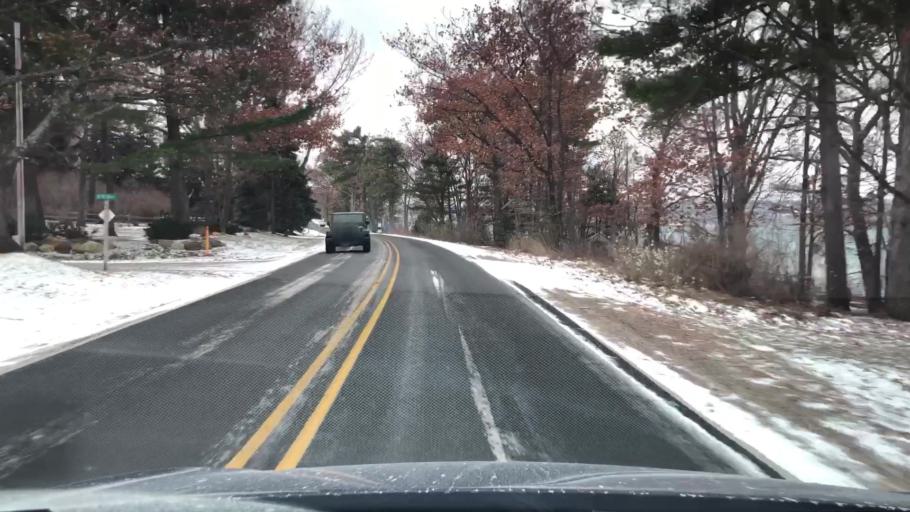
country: US
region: Michigan
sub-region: Grand Traverse County
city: Traverse City
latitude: 44.8119
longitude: -85.5793
